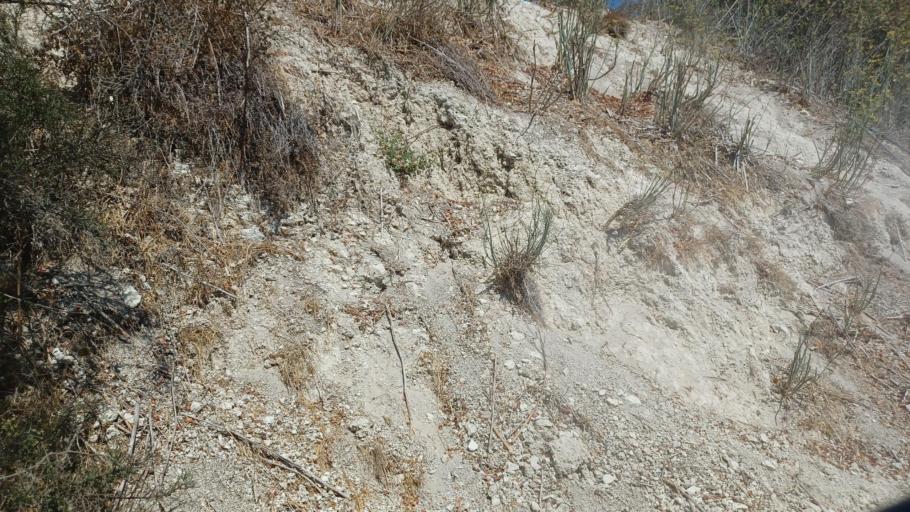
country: CY
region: Pafos
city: Mesogi
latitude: 34.8419
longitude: 32.5164
